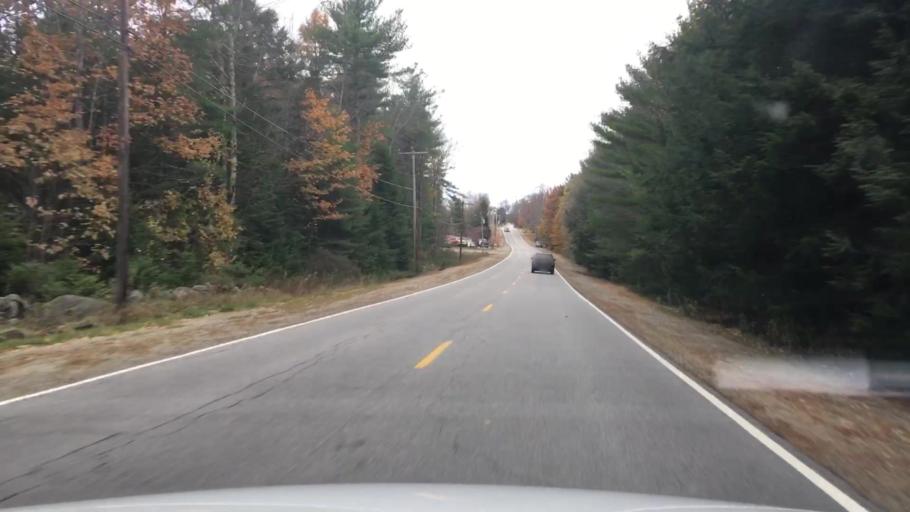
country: US
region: Maine
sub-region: Kennebec County
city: Monmouth
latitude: 44.1908
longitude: -70.0691
